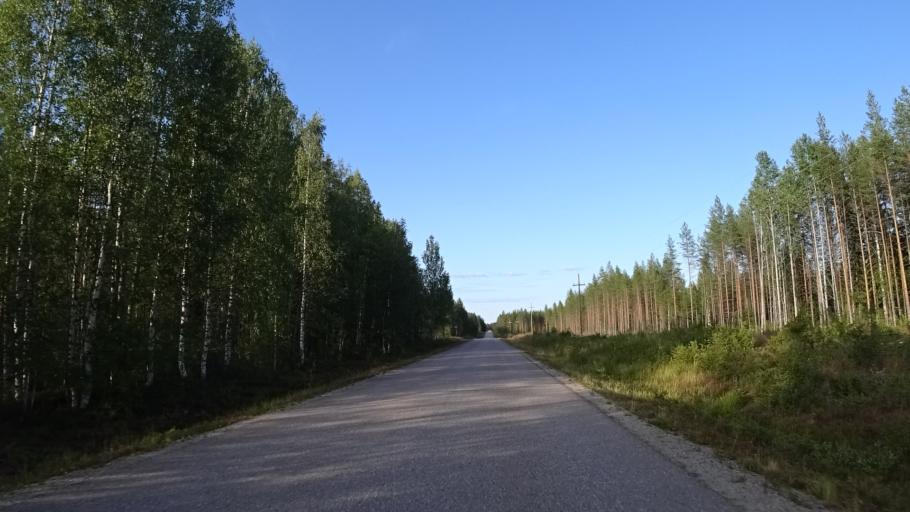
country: FI
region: North Karelia
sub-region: Joensuu
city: Eno
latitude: 63.0726
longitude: 30.5709
